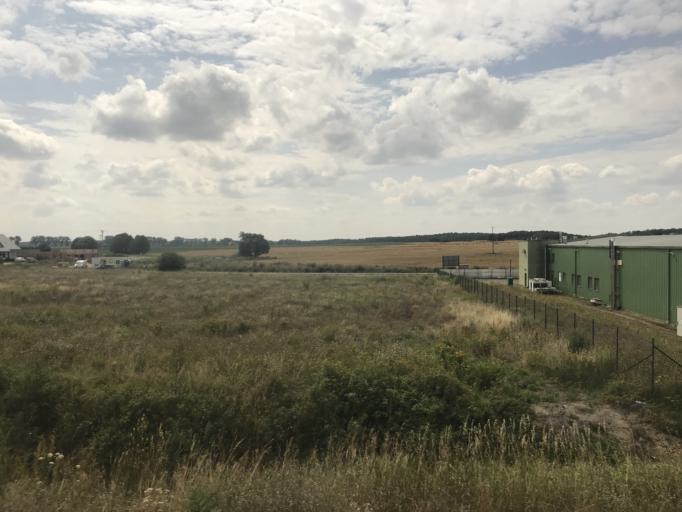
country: PL
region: Greater Poland Voivodeship
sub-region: Powiat poznanski
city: Pobiedziska
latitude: 52.4760
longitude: 17.2561
